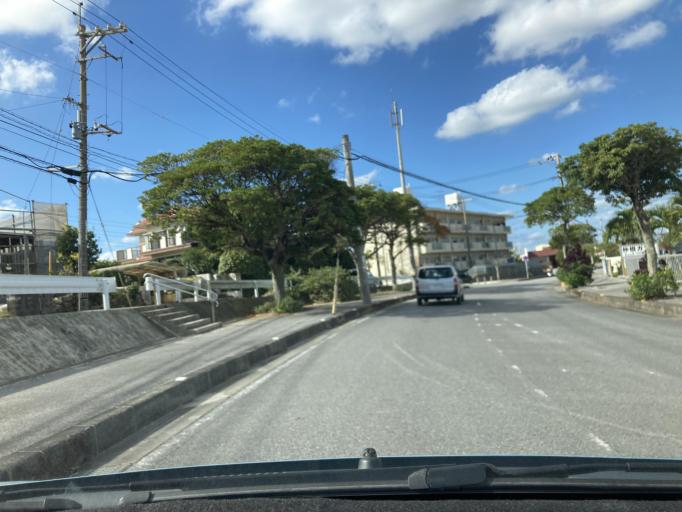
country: JP
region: Okinawa
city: Gushikawa
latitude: 26.3654
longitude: 127.8444
